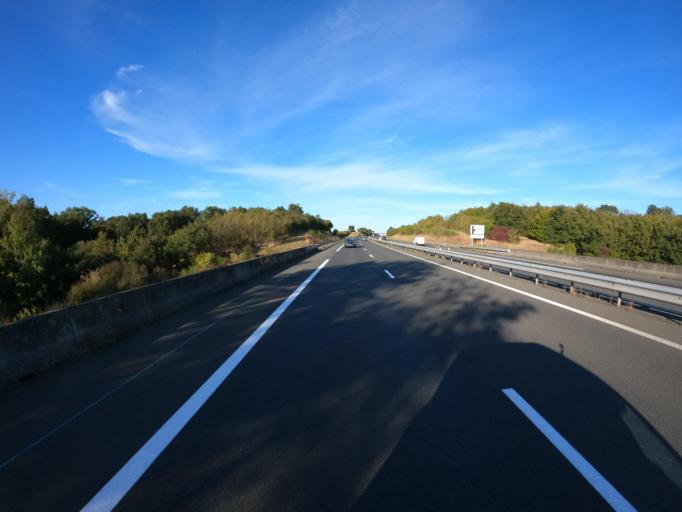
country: FR
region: Pays de la Loire
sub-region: Departement de Maine-et-Loire
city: Chemille-Melay
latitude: 47.2273
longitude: -0.7558
